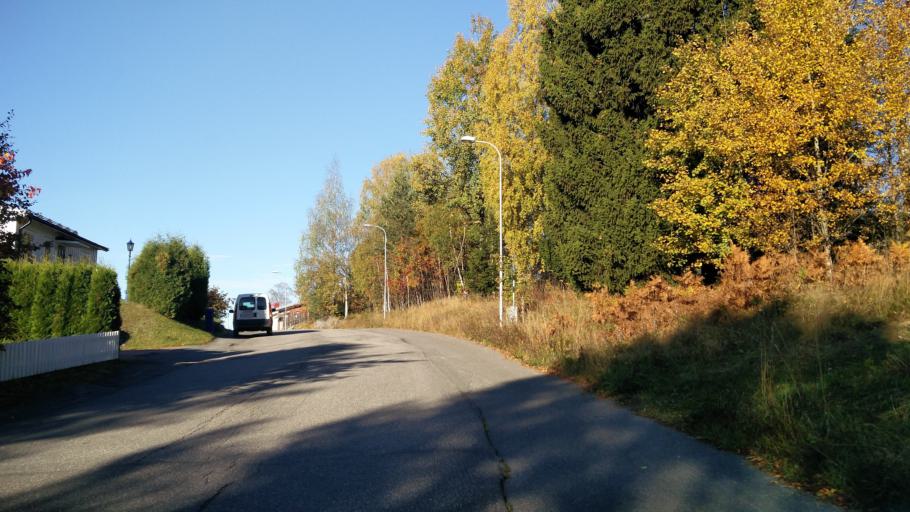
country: SE
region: Vaesternorrland
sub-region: Sundsvalls Kommun
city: Sundsvall
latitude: 62.4076
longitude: 17.2609
